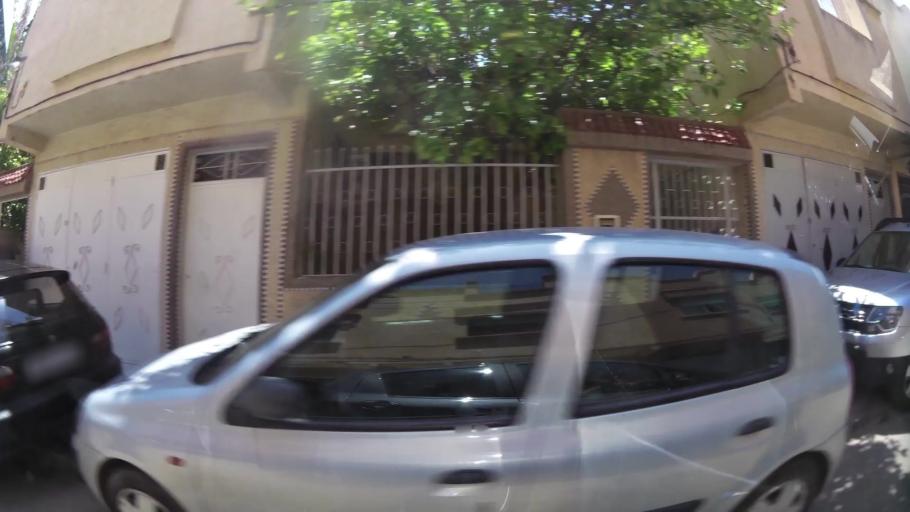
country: MA
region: Oriental
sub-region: Oujda-Angad
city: Oujda
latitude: 34.6952
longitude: -1.8976
